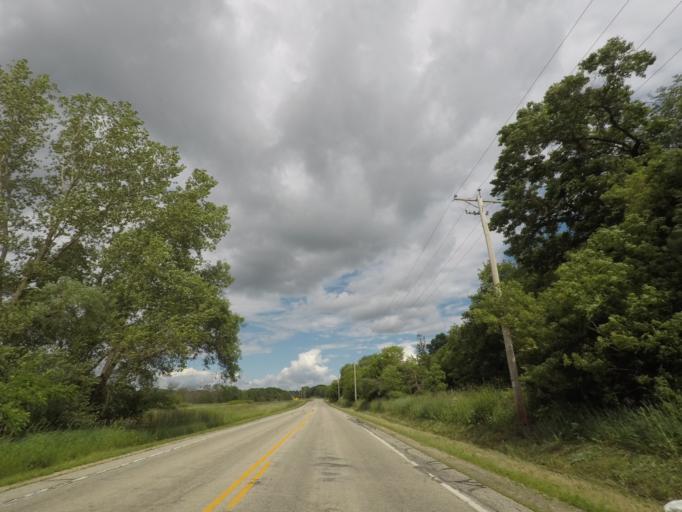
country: US
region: Wisconsin
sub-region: Green County
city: Brooklyn
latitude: 42.8270
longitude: -89.4379
